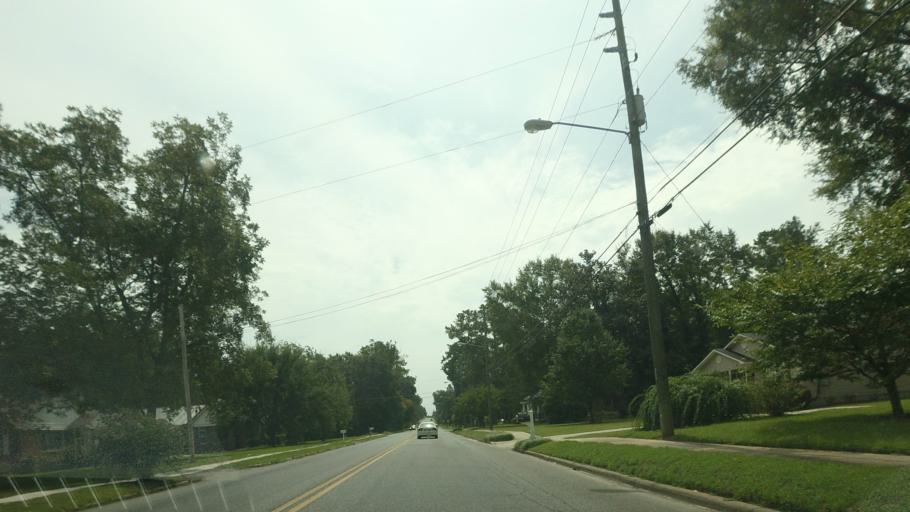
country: US
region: Georgia
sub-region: Bleckley County
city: Cochran
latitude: 32.3843
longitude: -83.3521
